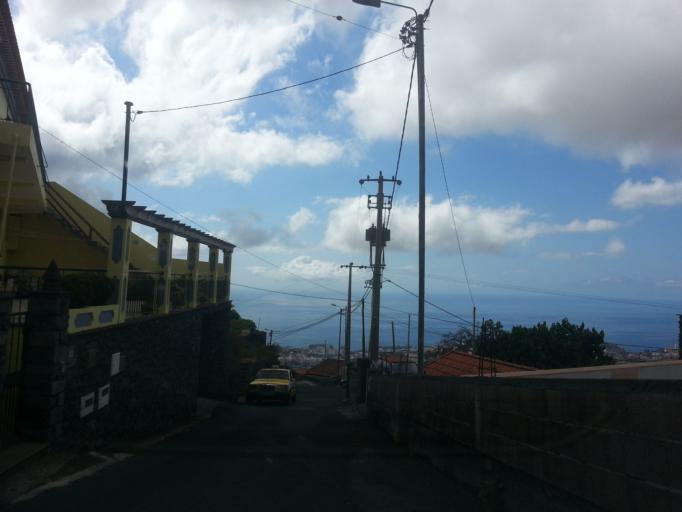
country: PT
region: Madeira
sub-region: Funchal
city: Nossa Senhora do Monte
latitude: 32.6791
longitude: -16.9387
